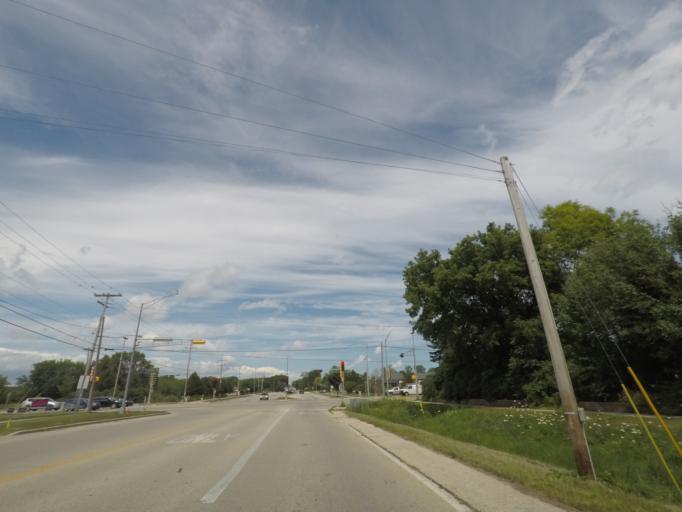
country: US
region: Wisconsin
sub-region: Milwaukee County
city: Greendale
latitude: 42.9155
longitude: -87.9795
